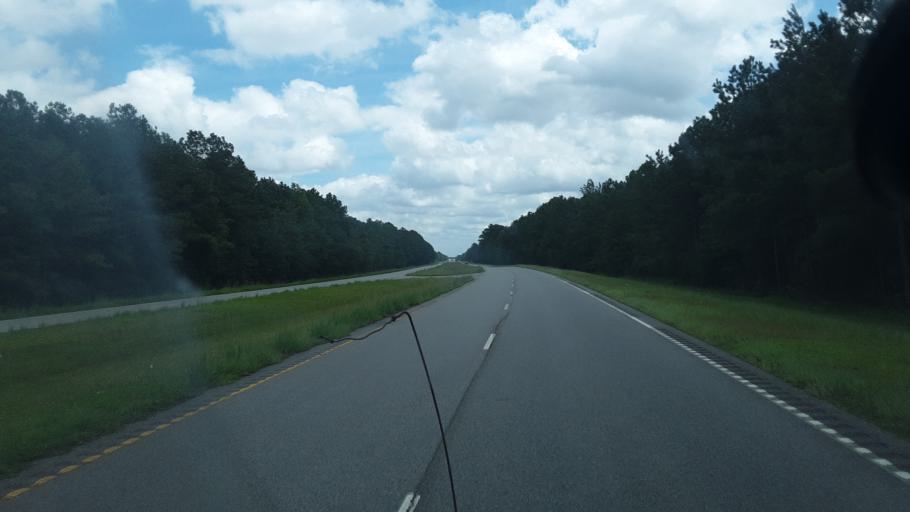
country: US
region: South Carolina
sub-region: Horry County
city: Loris
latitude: 34.0965
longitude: -78.9172
